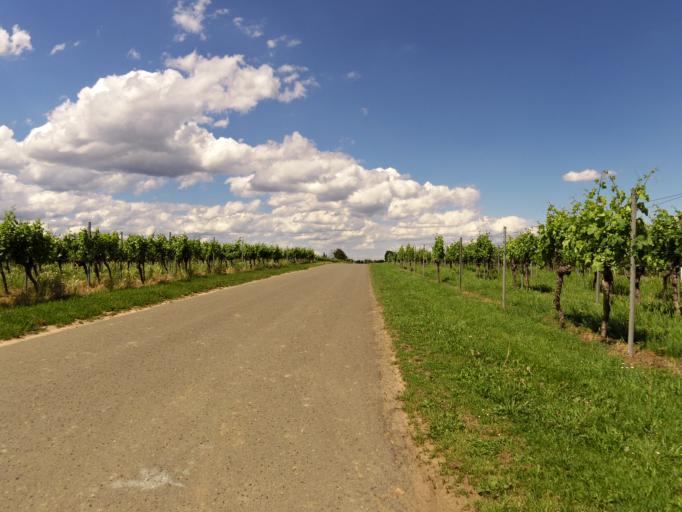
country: DE
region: Rheinland-Pfalz
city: Altdorf
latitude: 49.2905
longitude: 8.2148
